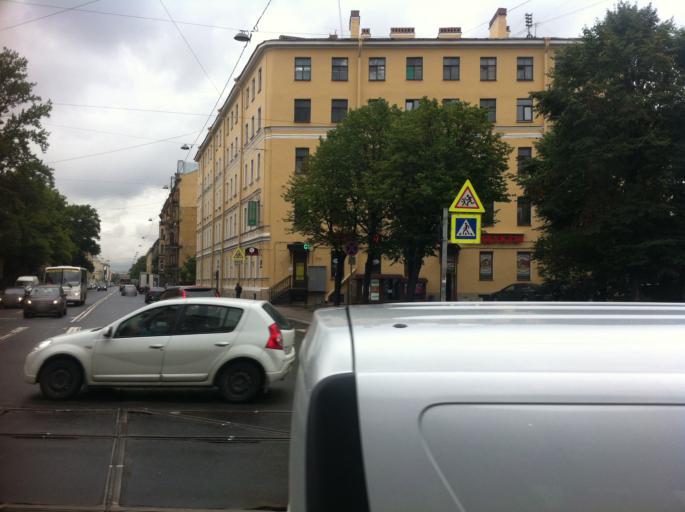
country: RU
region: St.-Petersburg
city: Admiralteisky
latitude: 59.9133
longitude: 30.2777
